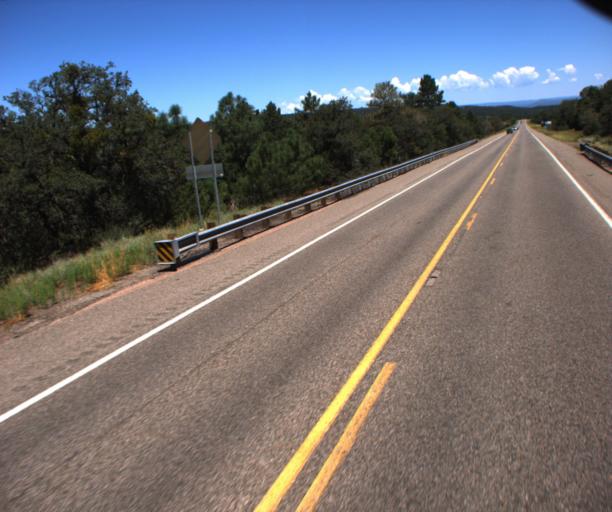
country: US
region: Arizona
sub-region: Gila County
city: San Carlos
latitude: 33.6612
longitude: -110.5720
